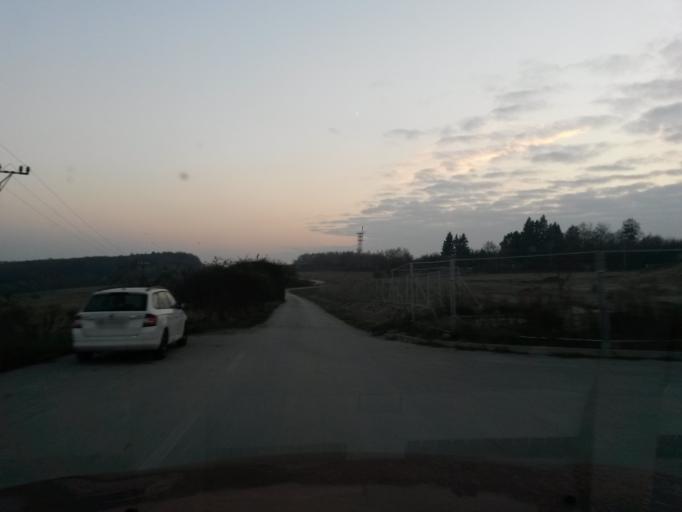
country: SK
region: Kosicky
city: Kosice
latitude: 48.7190
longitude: 21.2942
